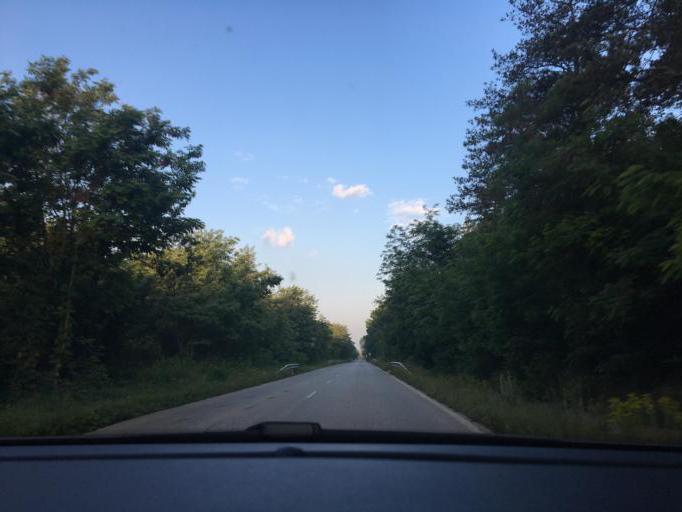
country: MK
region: Novo Selo
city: Novo Selo
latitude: 41.3963
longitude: 23.0088
